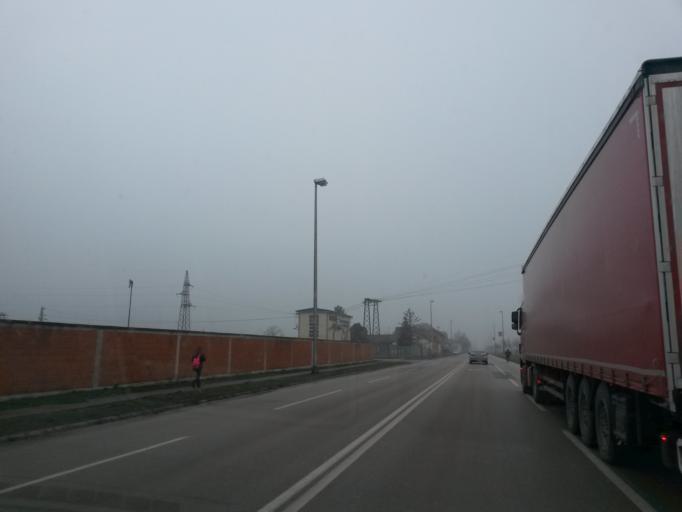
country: HR
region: Vukovarsko-Srijemska
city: Zupanja
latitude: 45.0896
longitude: 18.6968
